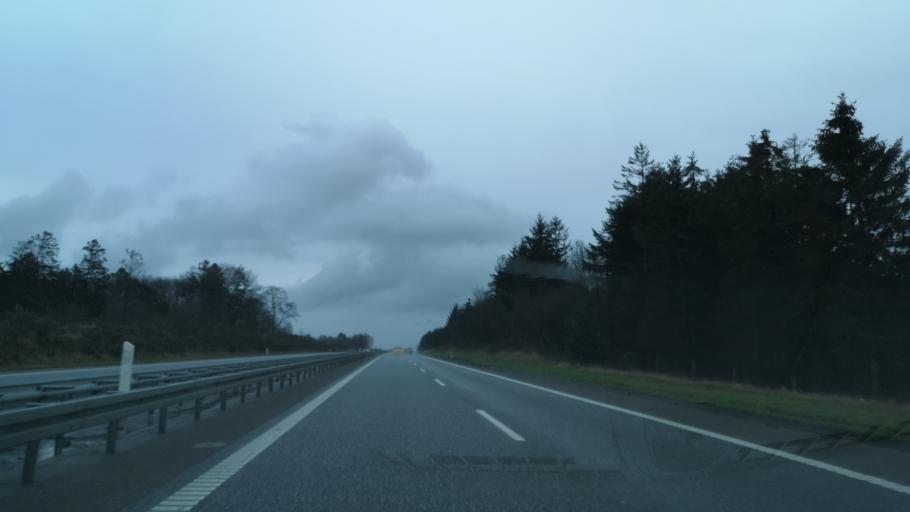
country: DK
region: South Denmark
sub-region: Vejle Kommune
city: Jelling
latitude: 55.8360
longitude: 9.3679
